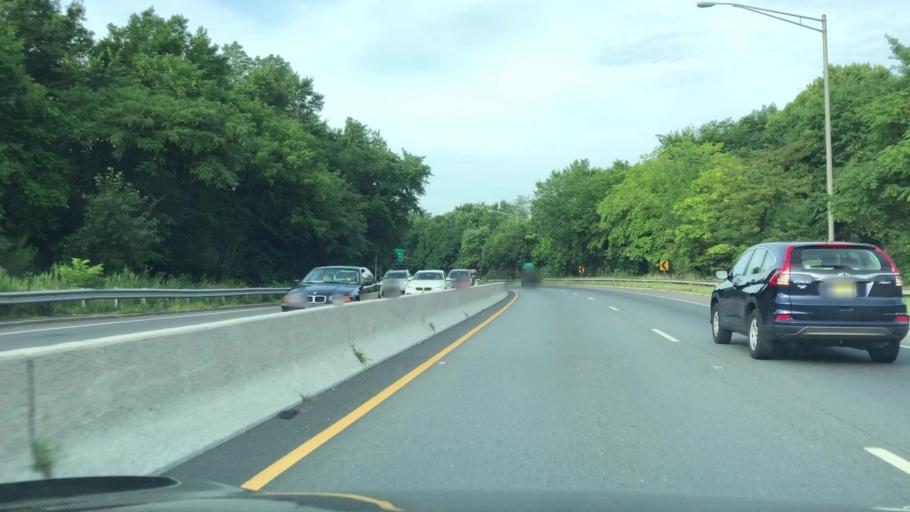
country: US
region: New Jersey
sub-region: Mercer County
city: Prospect Park
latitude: 40.2279
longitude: -74.7576
